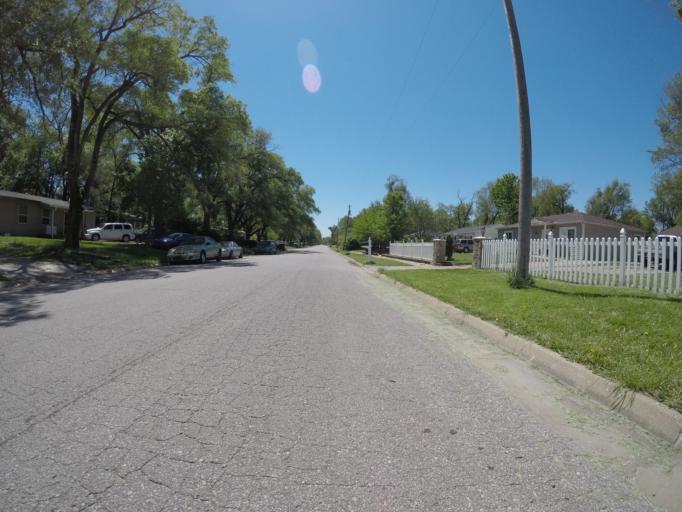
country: US
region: Kansas
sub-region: Shawnee County
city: Topeka
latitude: 39.0514
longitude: -95.6367
